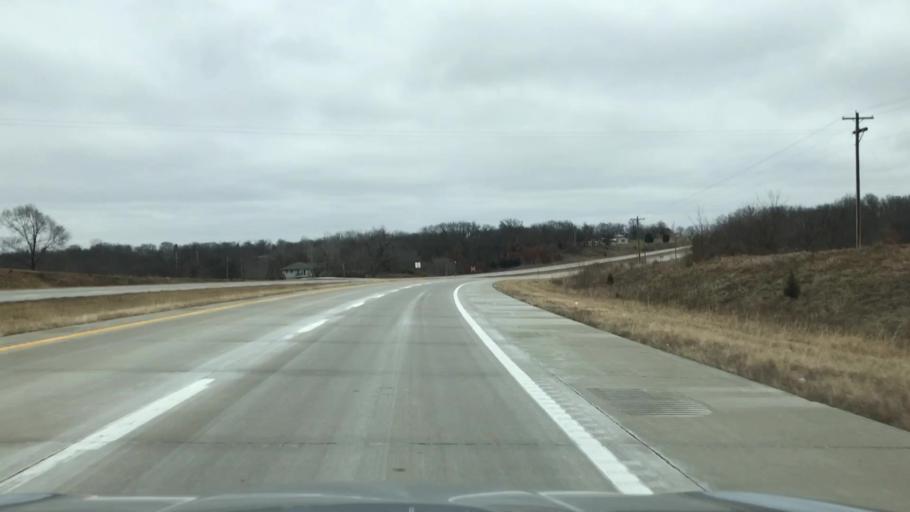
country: US
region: Missouri
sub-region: Livingston County
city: Chillicothe
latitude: 39.7400
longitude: -93.6425
